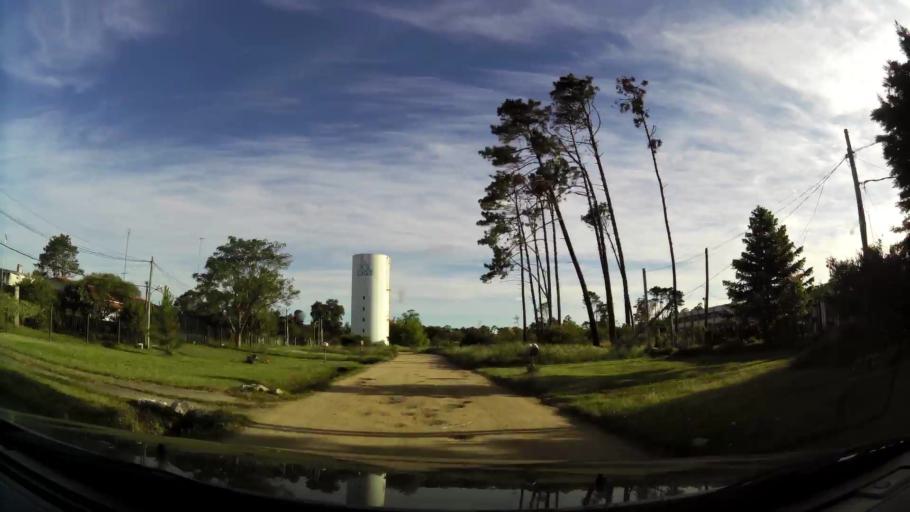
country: UY
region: Canelones
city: Empalme Olmos
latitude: -34.7749
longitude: -55.8578
